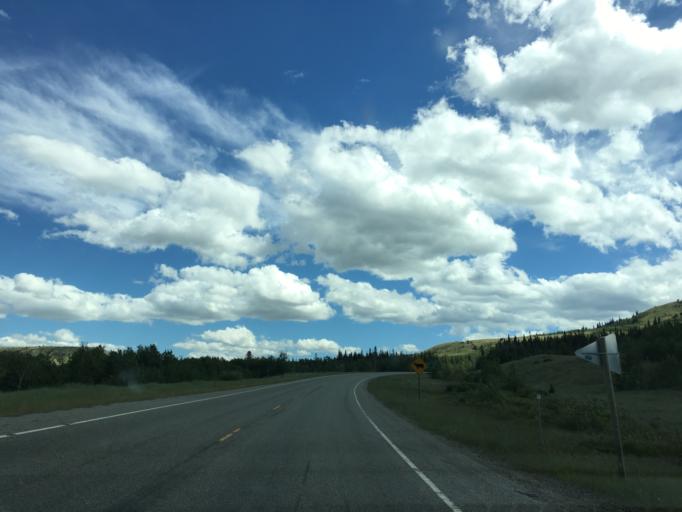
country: US
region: Montana
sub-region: Glacier County
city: Browning
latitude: 48.6079
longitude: -113.2865
